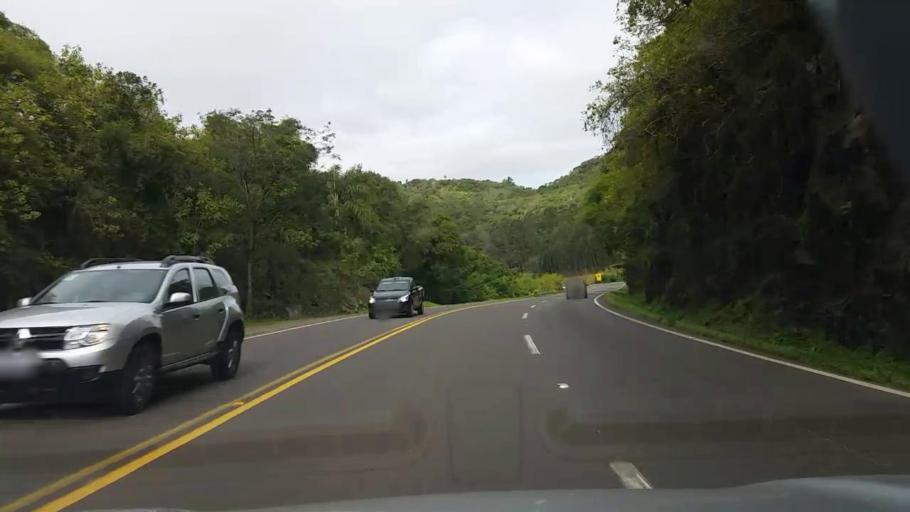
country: BR
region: Rio Grande do Sul
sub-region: Arroio Do Meio
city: Arroio do Meio
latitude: -29.3813
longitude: -52.0545
